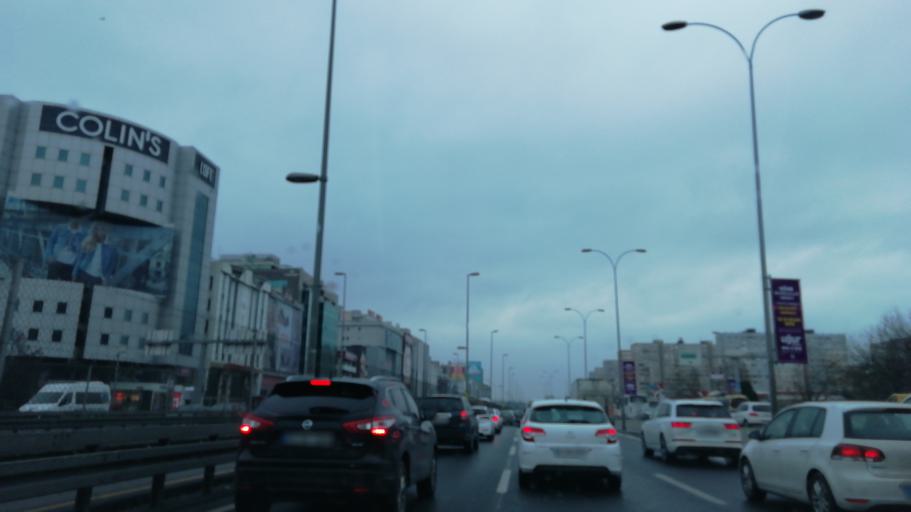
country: TR
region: Istanbul
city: Bahcelievler
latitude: 40.9922
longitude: 28.8362
